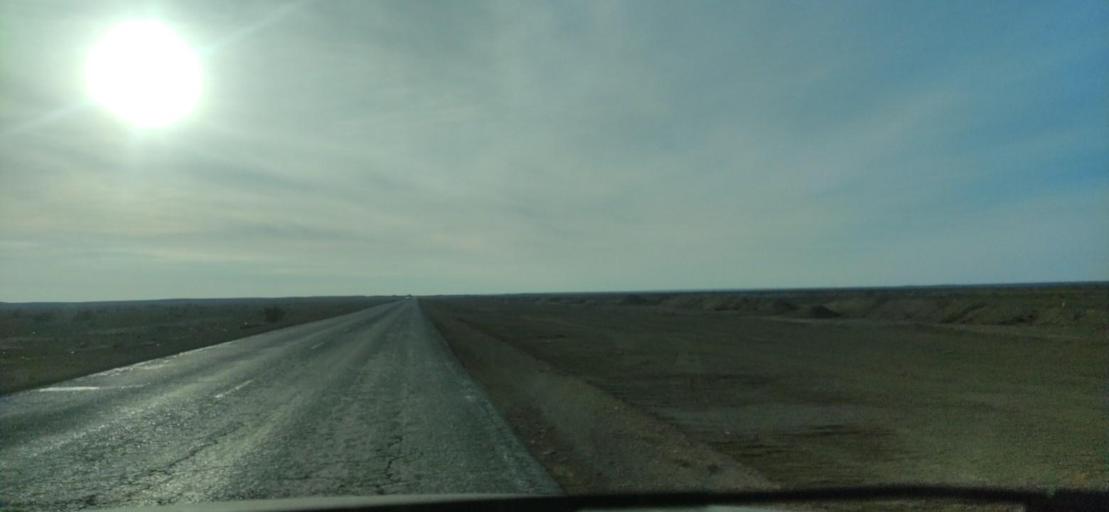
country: KZ
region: Qaraghandy
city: Saryshaghan
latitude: 46.3067
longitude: 73.7570
